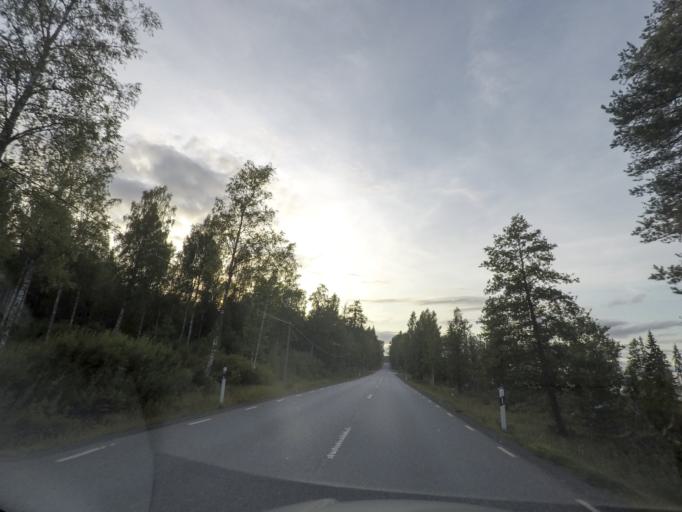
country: SE
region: OErebro
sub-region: Nora Kommun
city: As
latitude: 59.5619
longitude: 14.7384
